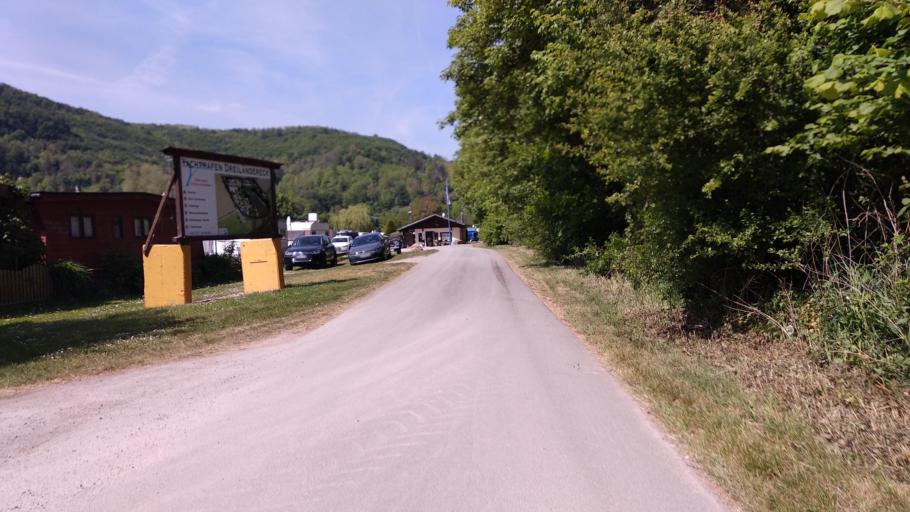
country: DE
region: North Rhine-Westphalia
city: Beverungen
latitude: 51.6504
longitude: 9.3809
